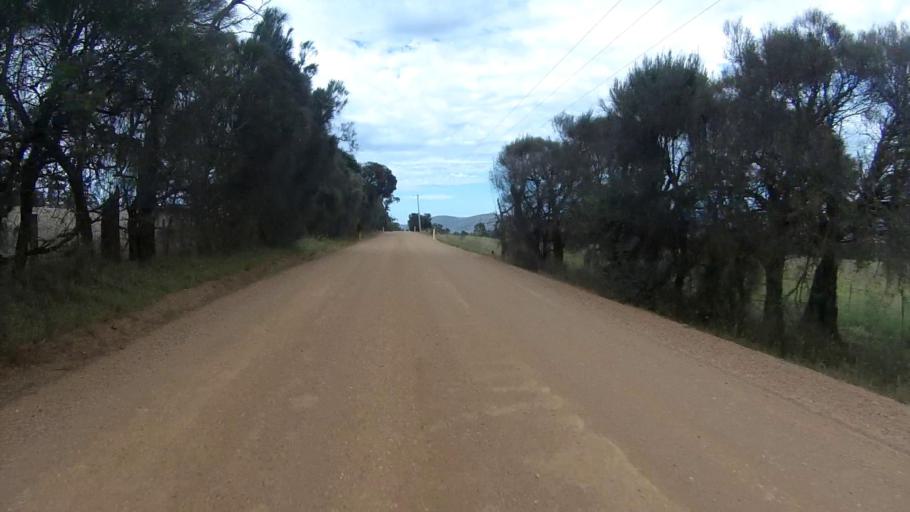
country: AU
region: Tasmania
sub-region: Clarence
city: Cambridge
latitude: -42.7034
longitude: 147.4575
